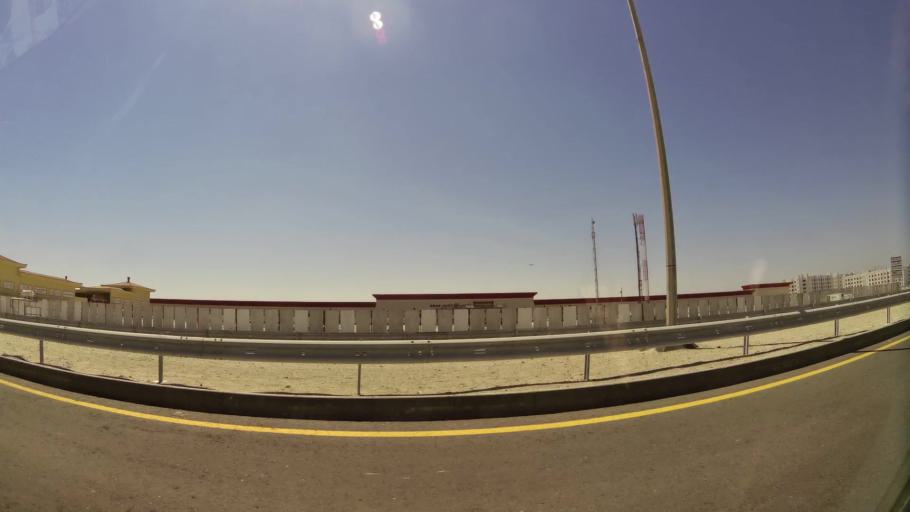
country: BH
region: Muharraq
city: Al Muharraq
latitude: 26.3078
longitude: 50.6265
